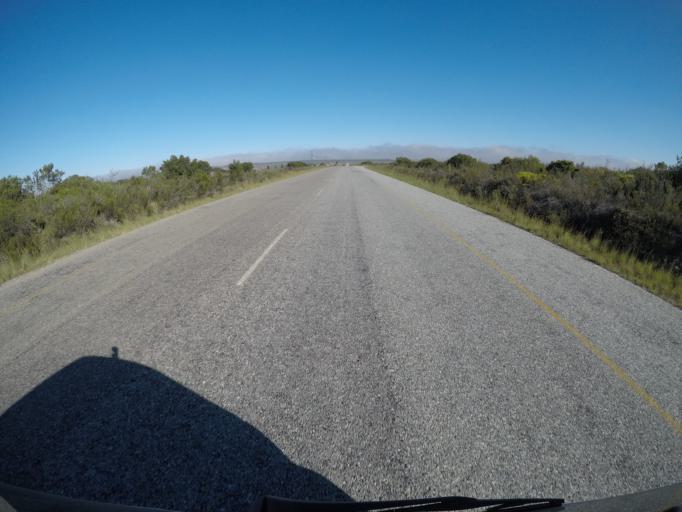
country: ZA
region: Western Cape
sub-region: Eden District Municipality
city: Mossel Bay
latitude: -34.1643
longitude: 22.0111
